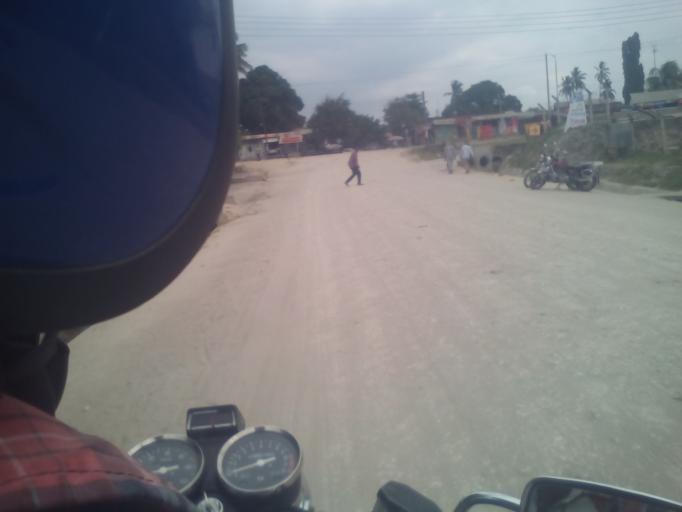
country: TZ
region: Dar es Salaam
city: Dar es Salaam
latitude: -6.8747
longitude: 39.2249
